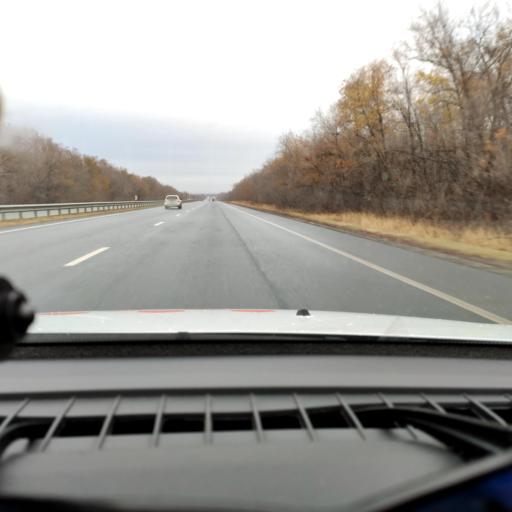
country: RU
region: Samara
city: Novokuybyshevsk
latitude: 53.0311
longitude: 49.9953
